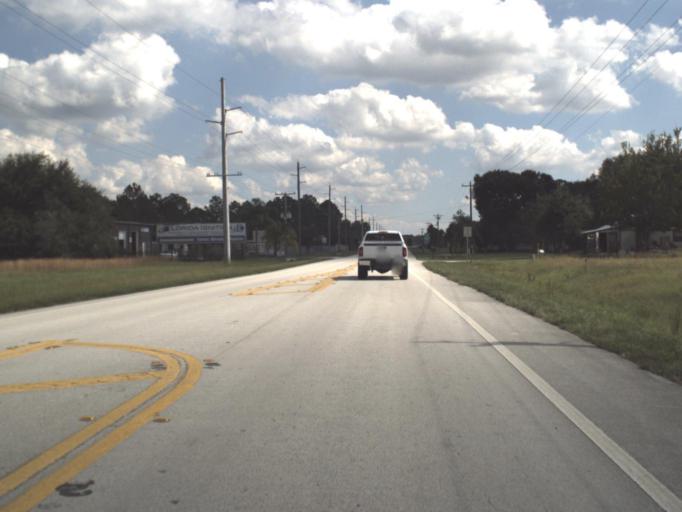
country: US
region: Florida
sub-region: Highlands County
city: Lake Placid
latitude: 27.4432
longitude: -81.2527
